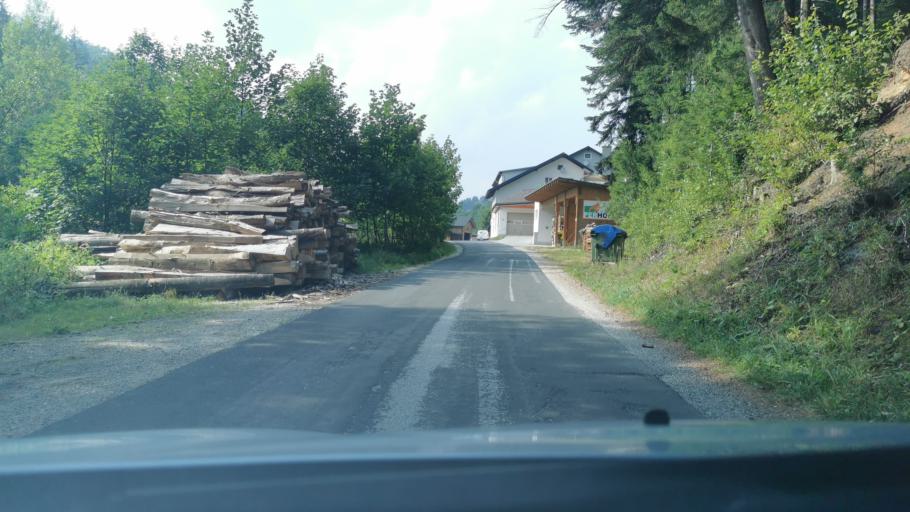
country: AT
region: Styria
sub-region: Politischer Bezirk Weiz
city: Fischbach
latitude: 47.3911
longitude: 15.6625
